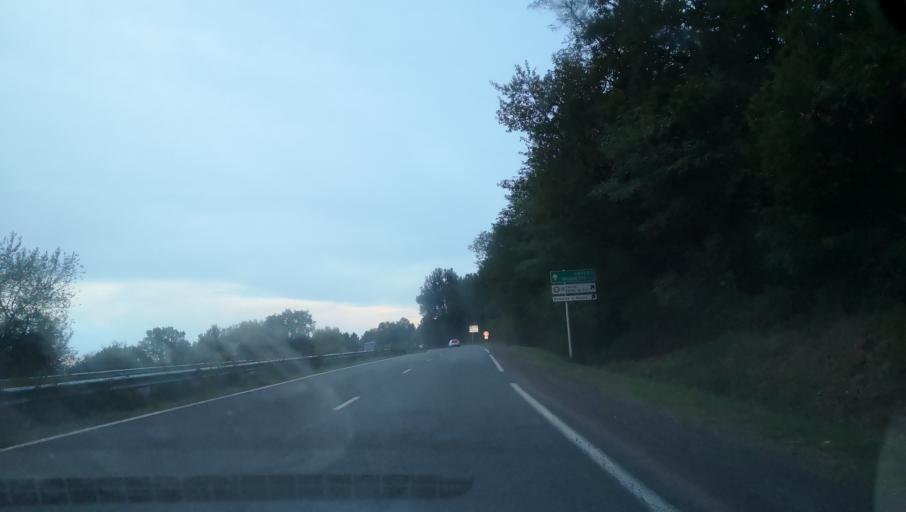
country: FR
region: Midi-Pyrenees
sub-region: Departement du Lot
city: Pradines
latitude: 44.5074
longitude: 1.4457
